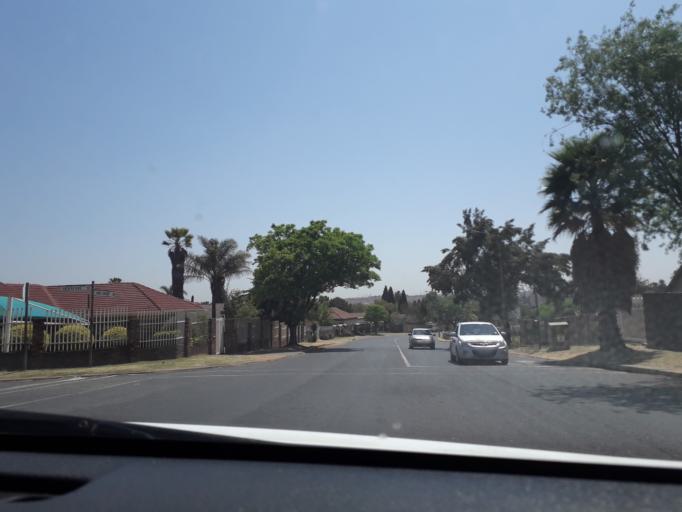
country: ZA
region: Gauteng
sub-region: Ekurhuleni Metropolitan Municipality
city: Tembisa
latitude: -26.0582
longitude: 28.2209
